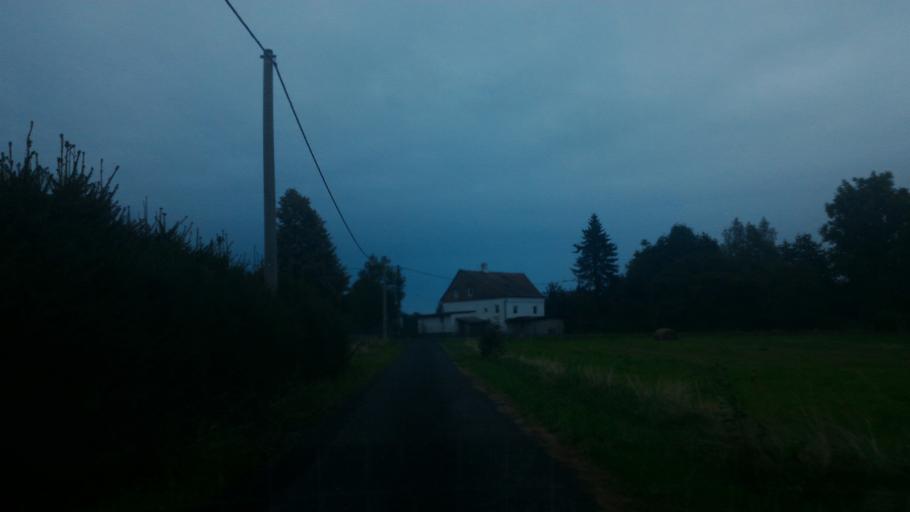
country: CZ
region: Ustecky
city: Dolni Podluzi
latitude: 50.9028
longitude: 14.5667
